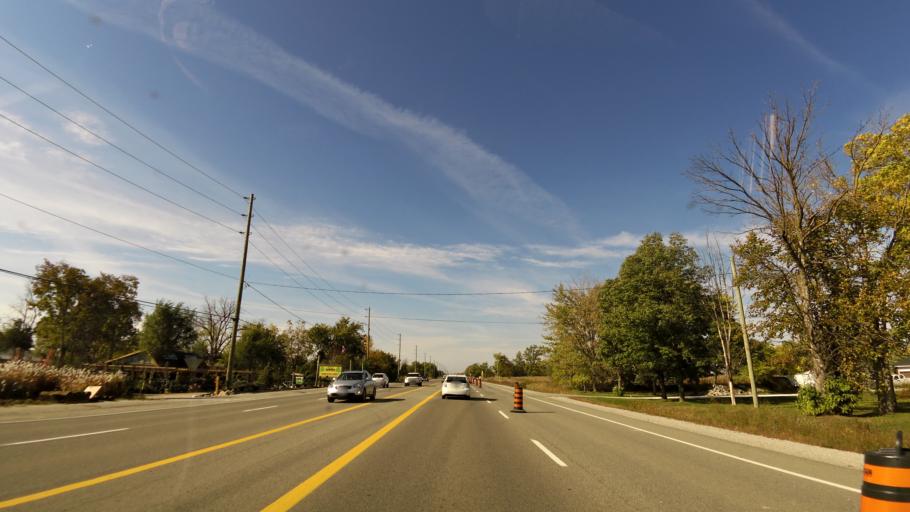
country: CA
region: Ontario
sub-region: Halton
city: Milton
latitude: 43.5485
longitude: -79.7988
